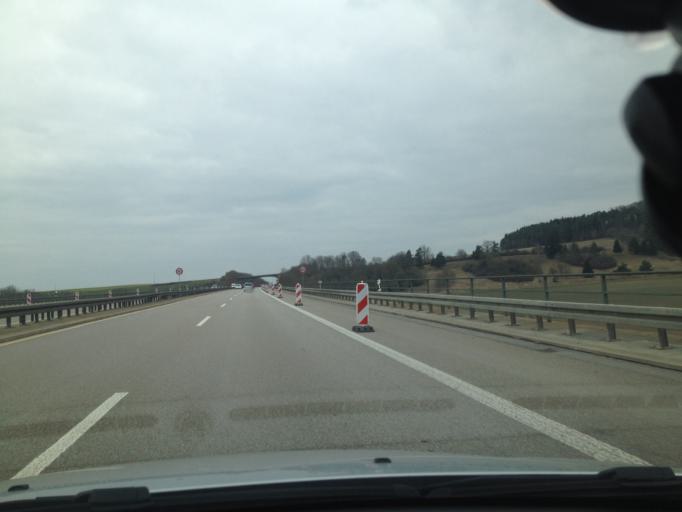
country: DE
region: Bavaria
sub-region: Regierungsbezirk Mittelfranken
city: Diebach
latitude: 49.3038
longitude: 10.2100
